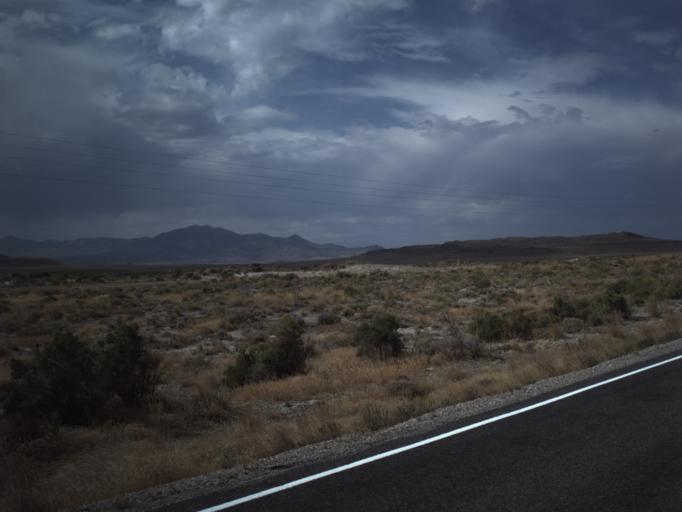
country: US
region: Utah
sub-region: Tooele County
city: Wendover
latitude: 41.4248
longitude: -113.8583
